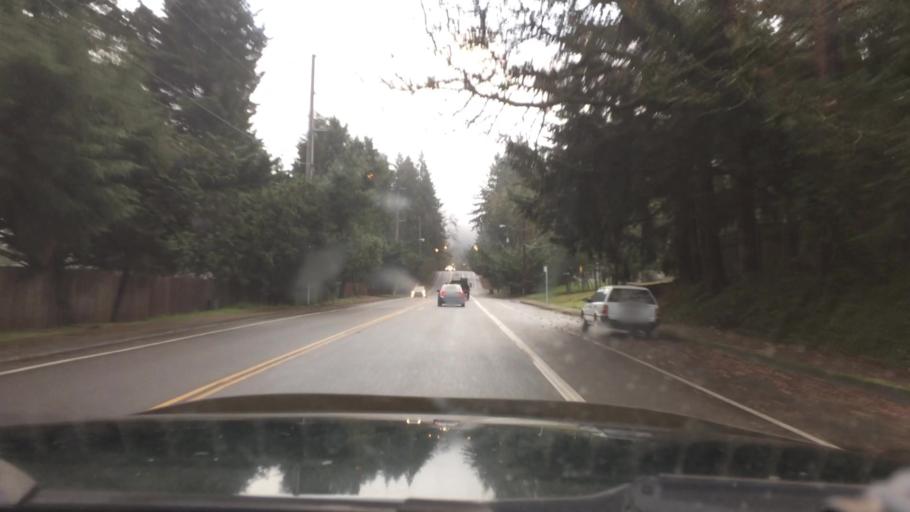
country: US
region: Oregon
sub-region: Lane County
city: Eugene
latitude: 44.0298
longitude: -123.1178
